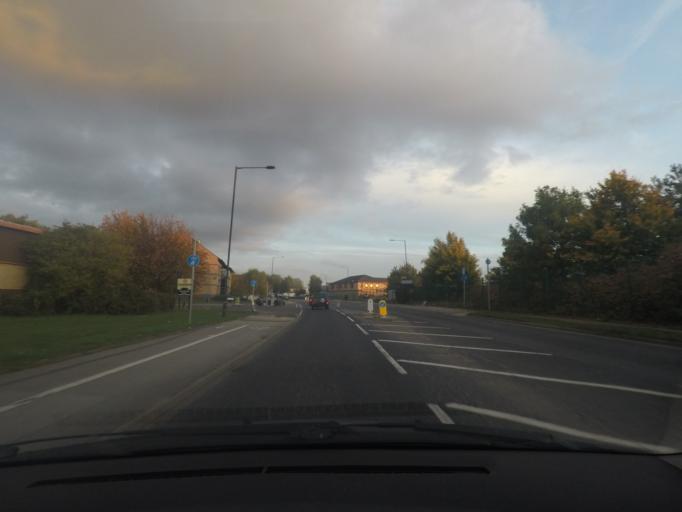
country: GB
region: England
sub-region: City of York
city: Skelton
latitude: 53.9867
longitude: -1.1026
